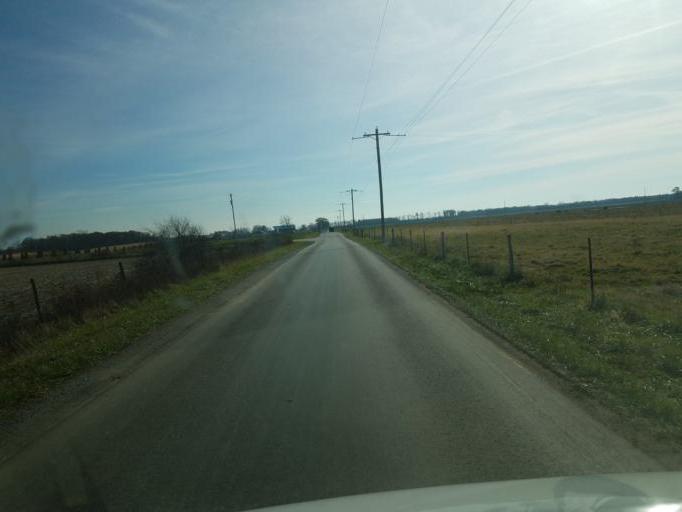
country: US
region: Ohio
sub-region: Hardin County
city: Kenton
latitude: 40.5738
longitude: -83.4529
